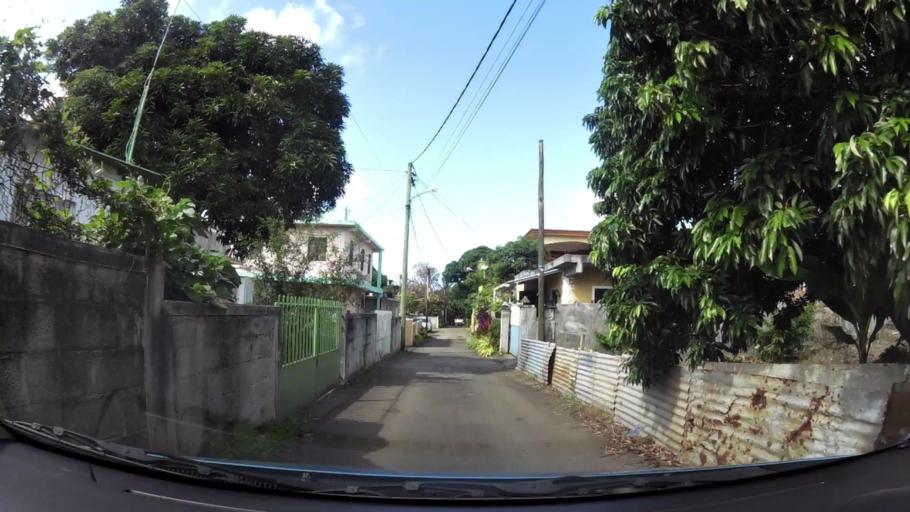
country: MU
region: Grand Port
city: Plaine Magnien
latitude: -20.4287
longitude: 57.6552
